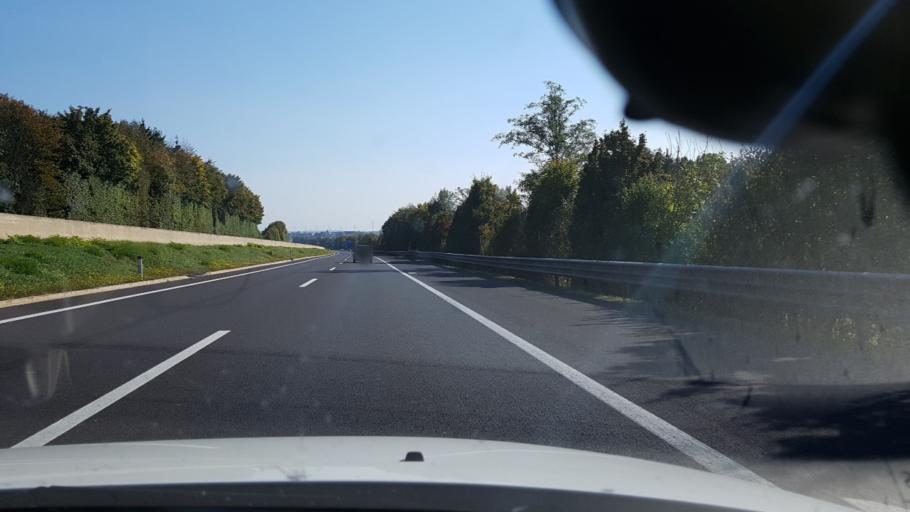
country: AT
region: Styria
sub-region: Politischer Bezirk Leibnitz
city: Wildon
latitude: 46.8648
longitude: 15.4951
